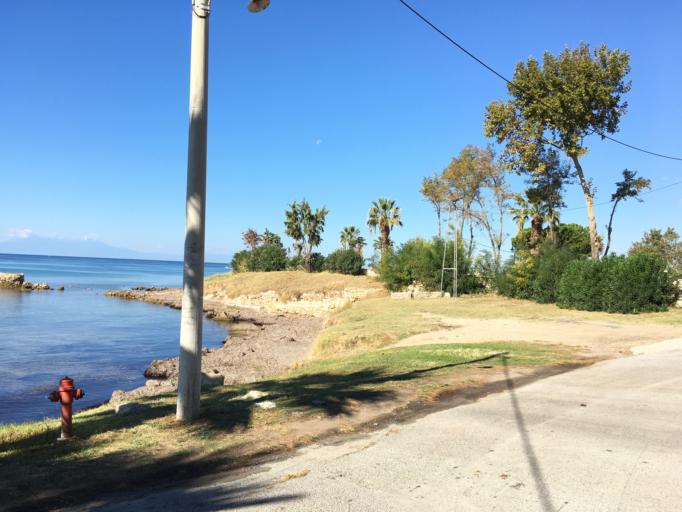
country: GR
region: Central Macedonia
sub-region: Nomos Chalkidikis
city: Nea Poteidaia
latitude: 40.1953
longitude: 23.3238
